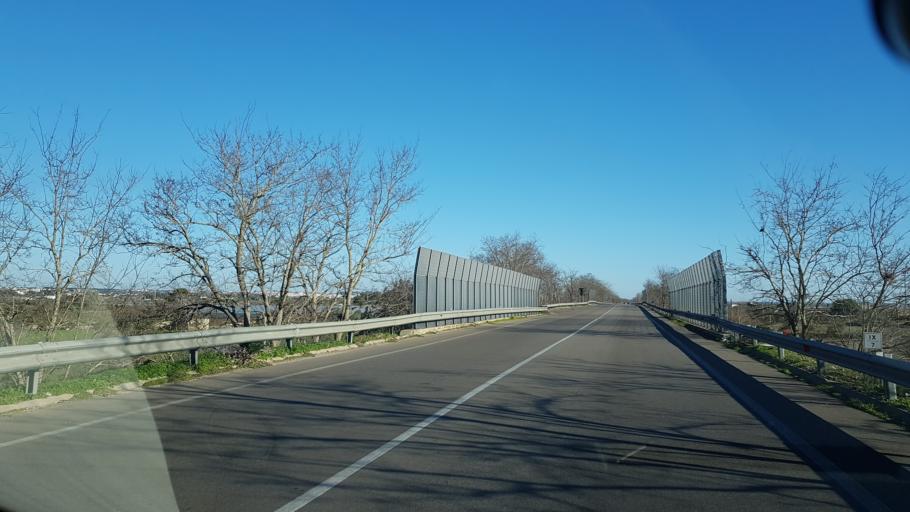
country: IT
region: Apulia
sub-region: Provincia di Lecce
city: Taviano
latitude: 39.9971
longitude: 18.0838
